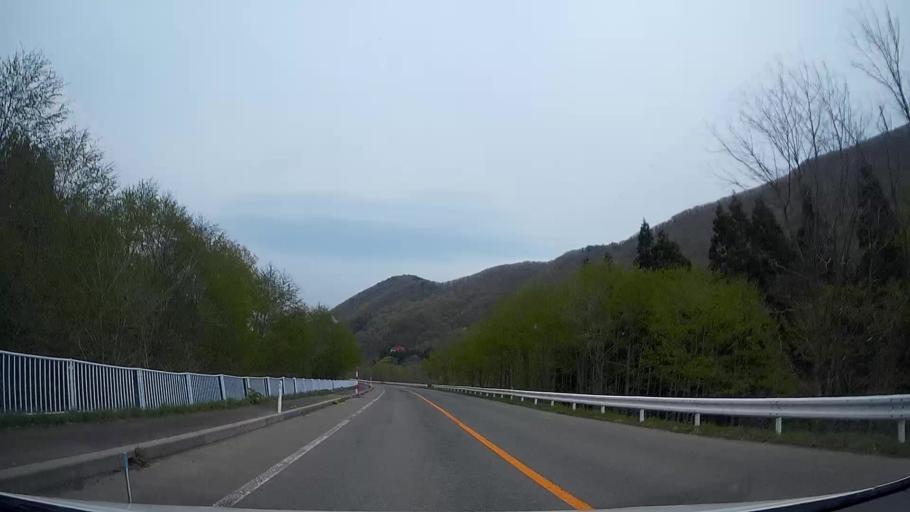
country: JP
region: Akita
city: Hanawa
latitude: 40.3482
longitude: 140.8420
